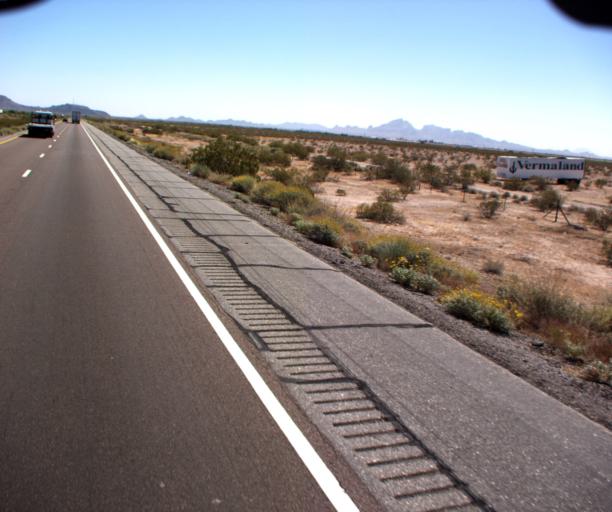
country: US
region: Arizona
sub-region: La Paz County
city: Salome
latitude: 33.5439
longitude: -113.1898
